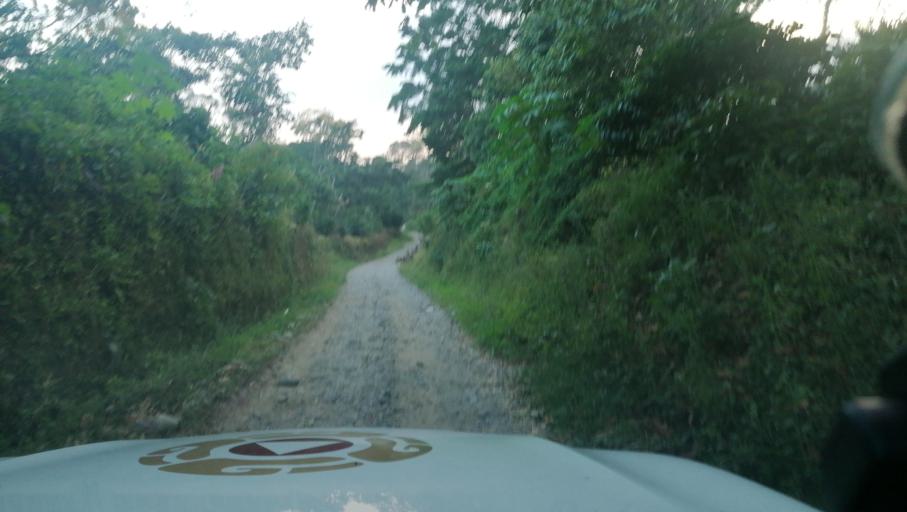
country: MX
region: Chiapas
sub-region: Cacahoatan
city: Benito Juarez
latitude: 15.0843
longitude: -92.2223
